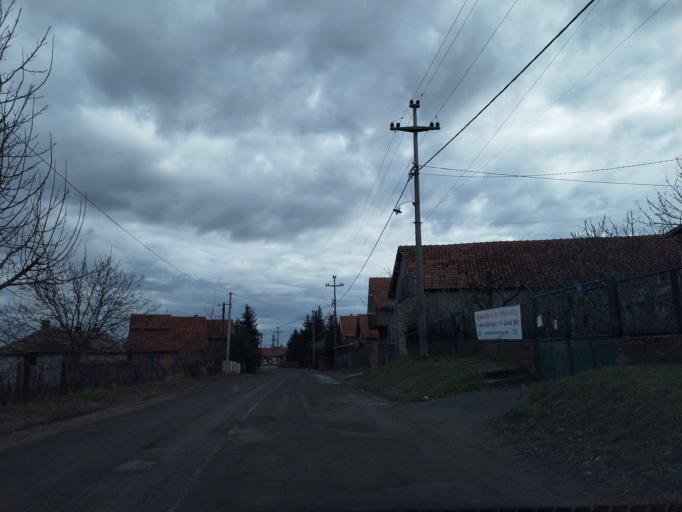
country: RS
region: Central Serbia
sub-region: Belgrade
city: Grocka
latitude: 44.6148
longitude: 20.7260
